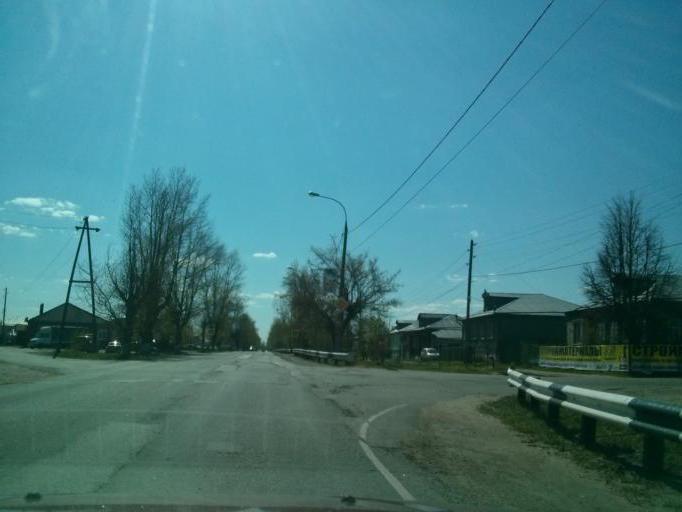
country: RU
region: Nizjnij Novgorod
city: Vorsma
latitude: 55.9940
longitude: 43.2845
